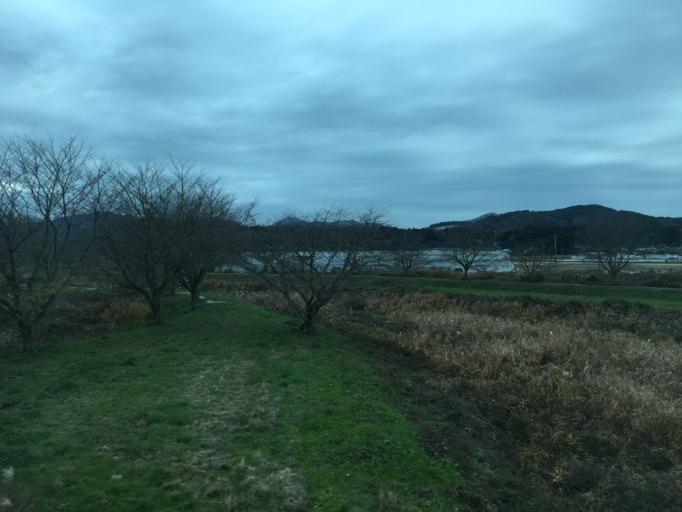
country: JP
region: Ibaraki
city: Kasama
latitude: 36.3738
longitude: 140.2438
